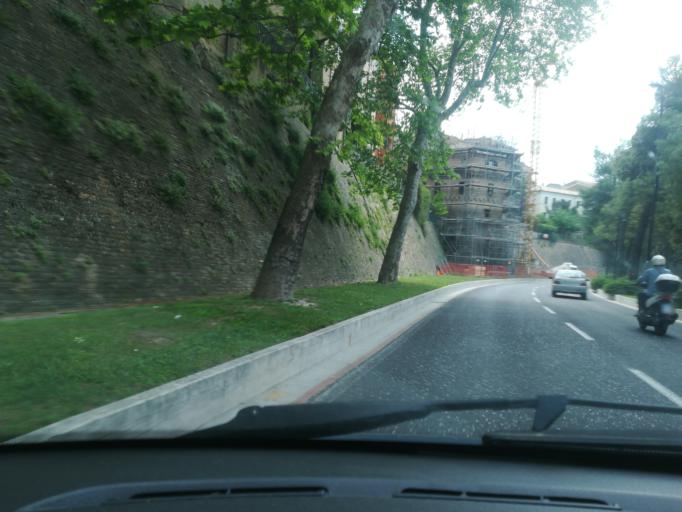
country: IT
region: The Marches
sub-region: Provincia di Macerata
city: Macerata
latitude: 43.3000
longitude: 13.4483
